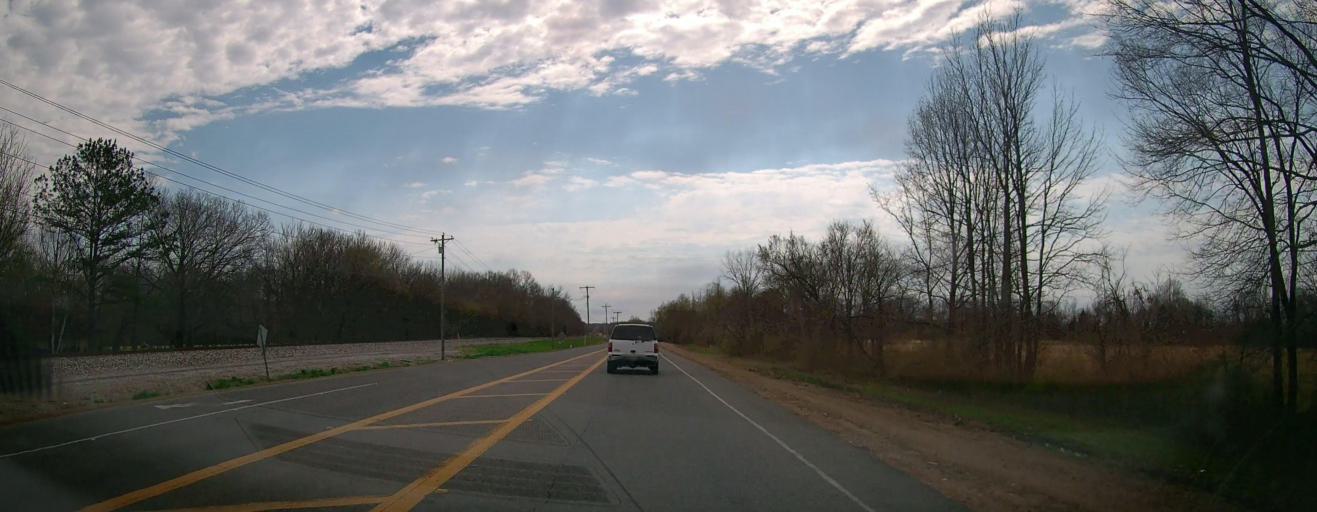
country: US
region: Mississippi
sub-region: De Soto County
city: Olive Branch
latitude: 34.9164
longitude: -89.7665
